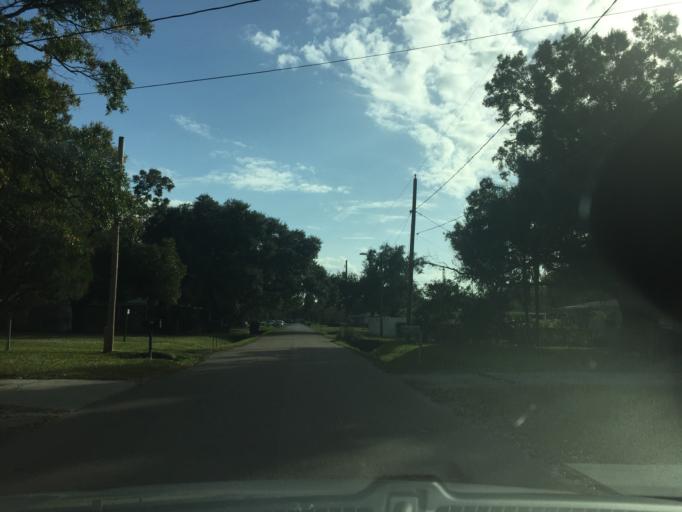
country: US
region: Florida
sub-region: Hillsborough County
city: Tampa
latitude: 27.9505
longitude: -82.4902
